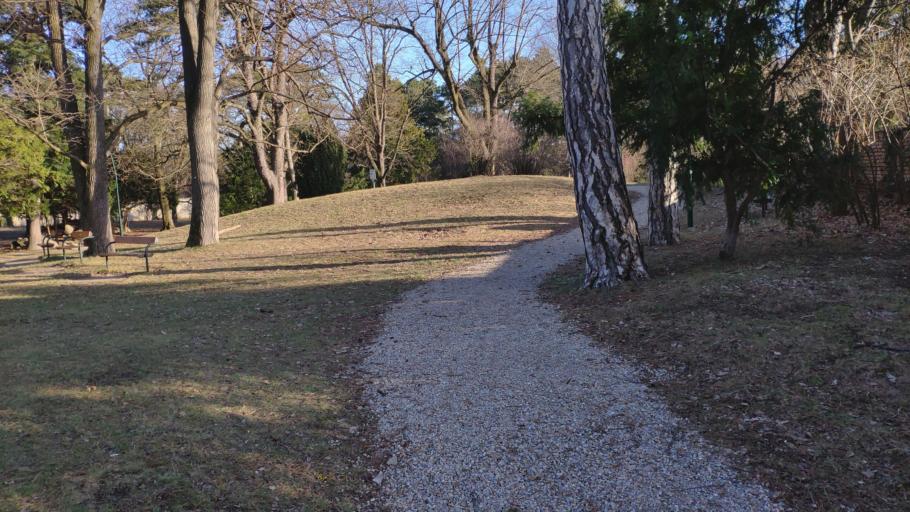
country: AT
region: Lower Austria
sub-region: Politischer Bezirk Modling
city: Perchtoldsdorf
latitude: 48.1776
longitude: 16.2999
